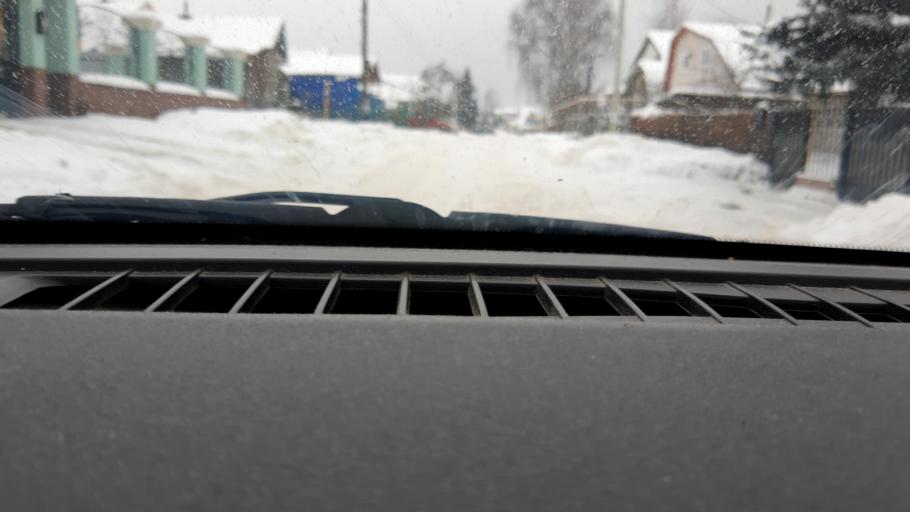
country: RU
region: Nizjnij Novgorod
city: Afonino
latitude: 56.1941
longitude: 44.0619
